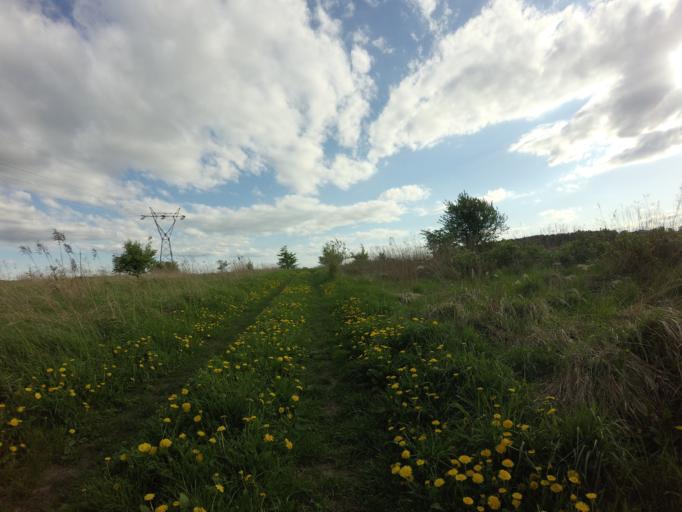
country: PL
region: West Pomeranian Voivodeship
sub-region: Powiat choszczenski
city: Choszczno
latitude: 53.1645
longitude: 15.3917
